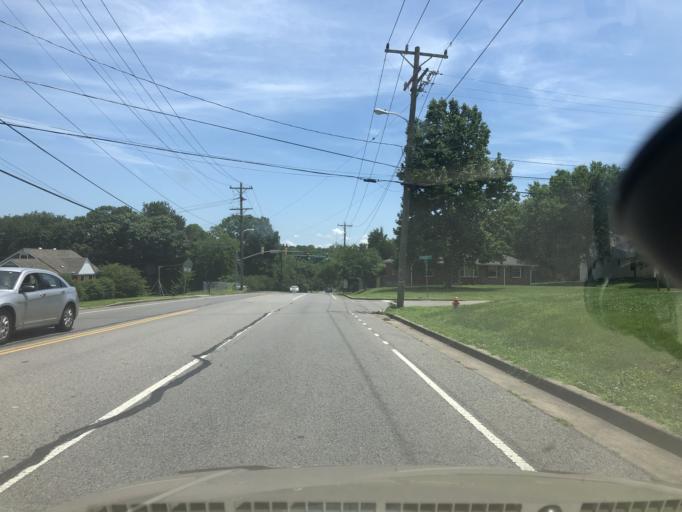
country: US
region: Tennessee
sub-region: Davidson County
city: Lakewood
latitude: 36.2525
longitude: -86.6950
